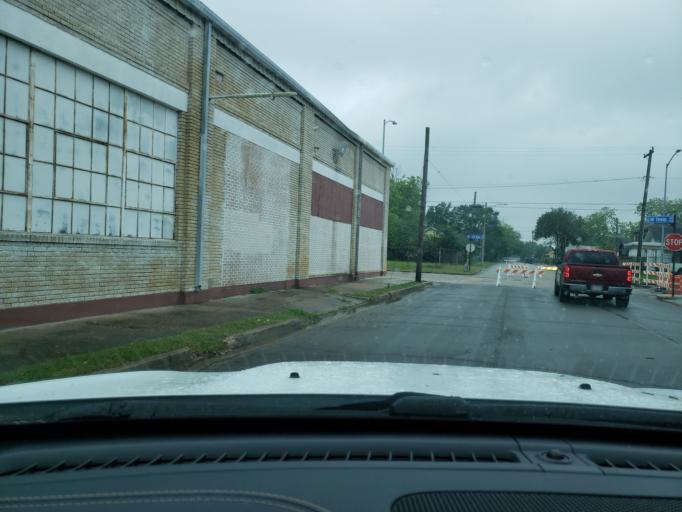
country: US
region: Texas
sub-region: Harris County
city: Baytown
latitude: 29.7344
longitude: -94.9737
